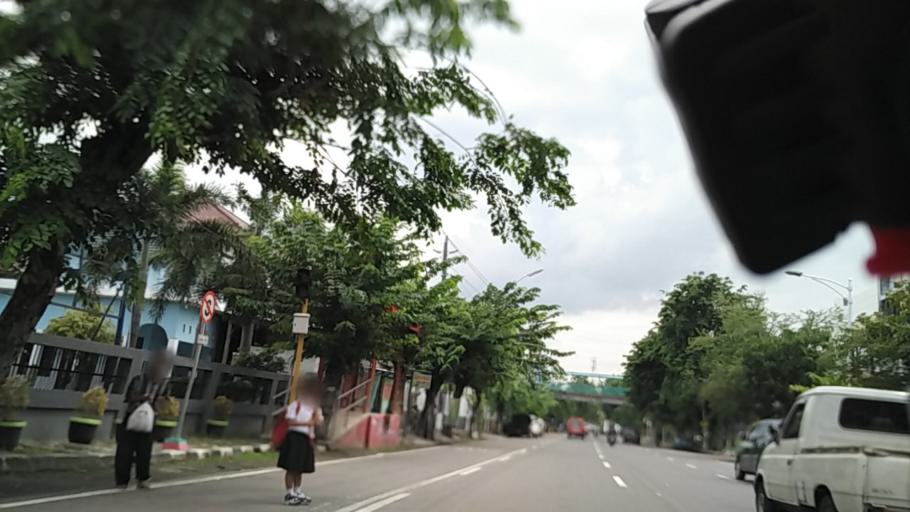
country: ID
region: Central Java
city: Semarang
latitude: -6.9741
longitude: 110.4346
